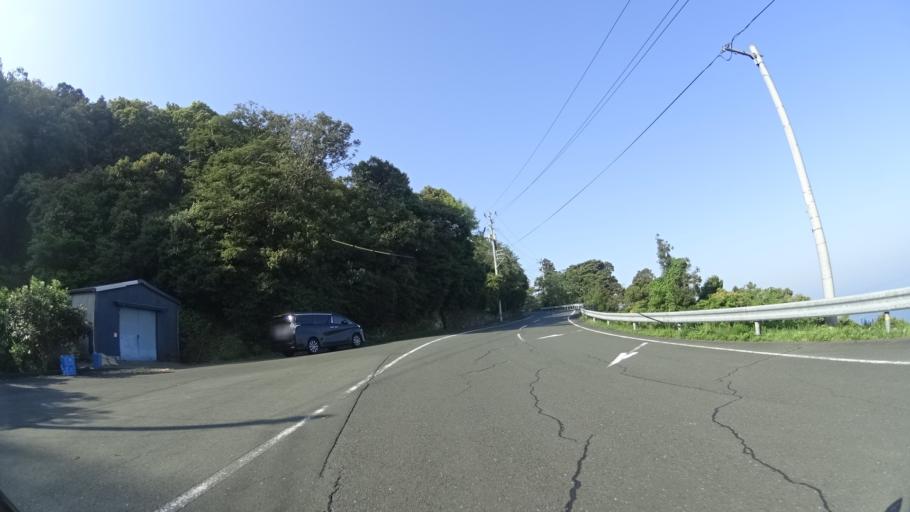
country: JP
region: Ehime
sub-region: Nishiuwa-gun
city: Ikata-cho
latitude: 33.3657
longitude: 132.0405
